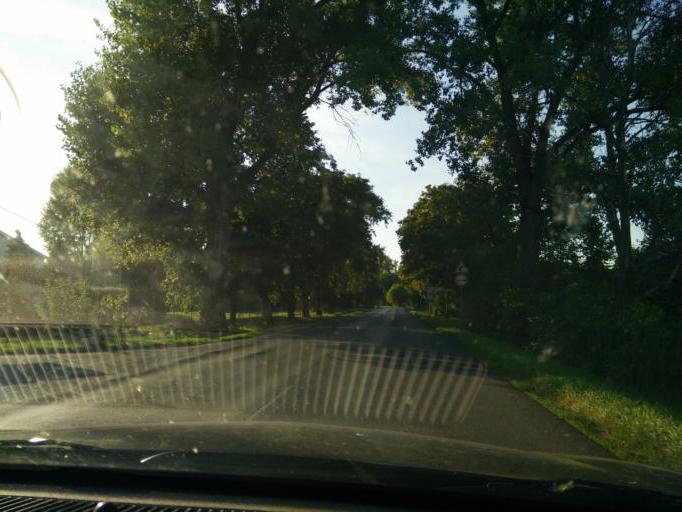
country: HU
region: Pest
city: Zsambek
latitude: 47.5367
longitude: 18.7248
